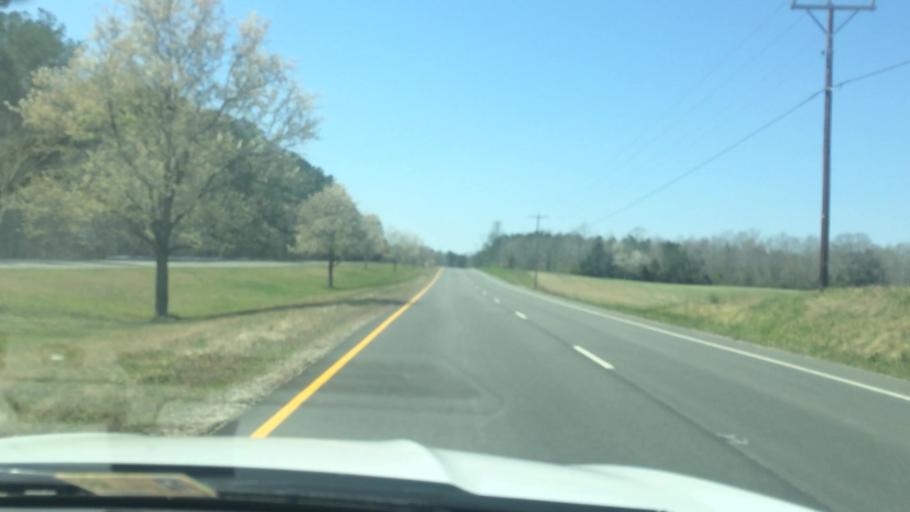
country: US
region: Virginia
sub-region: Middlesex County
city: Saluda
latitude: 37.5995
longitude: -76.5747
